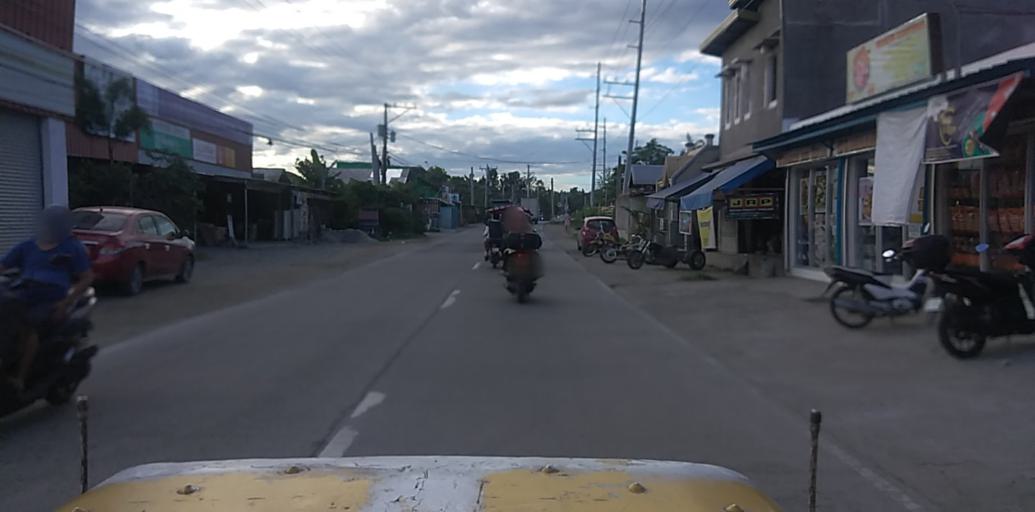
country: PH
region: Central Luzon
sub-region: Province of Pampanga
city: Arayat
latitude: 15.1479
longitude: 120.7602
